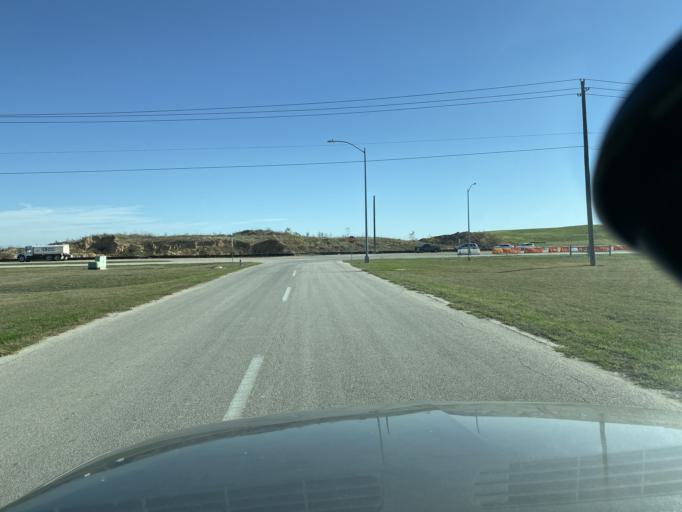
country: US
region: Texas
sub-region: Travis County
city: Hornsby Bend
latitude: 30.1956
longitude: -97.6637
